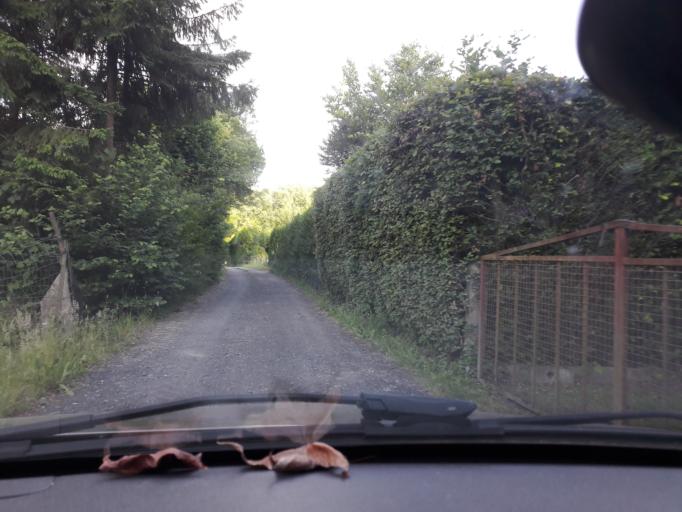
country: BE
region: Wallonia
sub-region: Province du Hainaut
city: Beaumont
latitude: 50.2601
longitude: 4.1790
